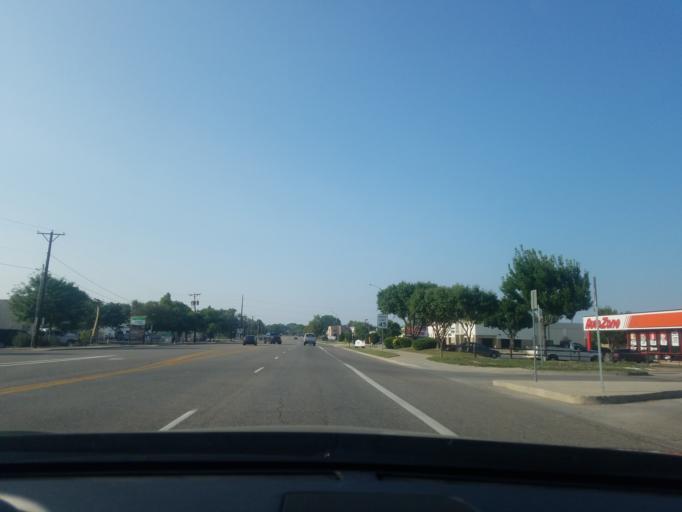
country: US
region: Colorado
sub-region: Larimer County
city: Loveland
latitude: 40.3789
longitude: -105.0732
